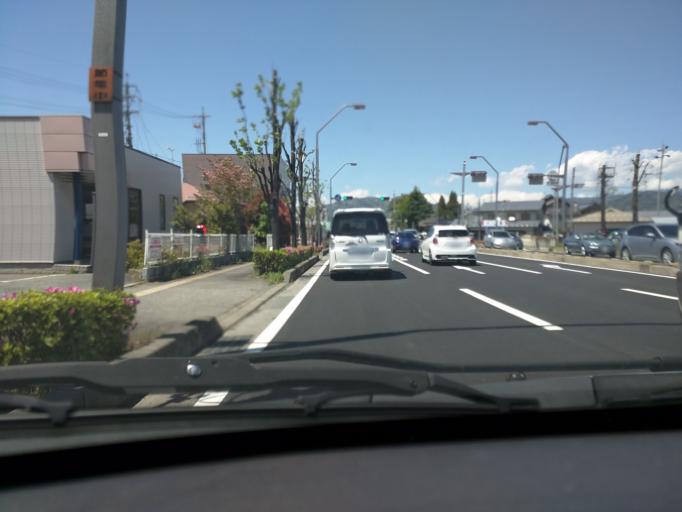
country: JP
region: Nagano
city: Suzaka
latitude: 36.6417
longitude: 138.2504
